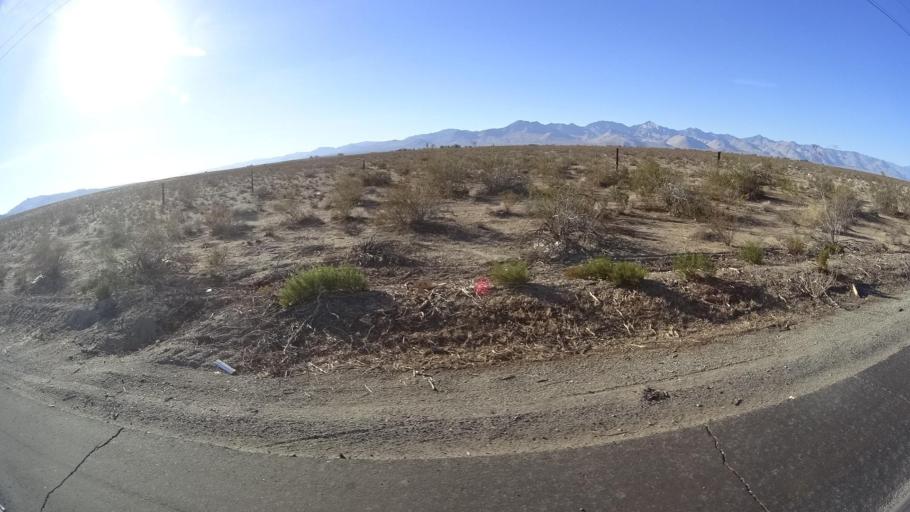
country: US
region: California
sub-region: Kern County
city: China Lake Acres
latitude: 35.6287
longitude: -117.7229
